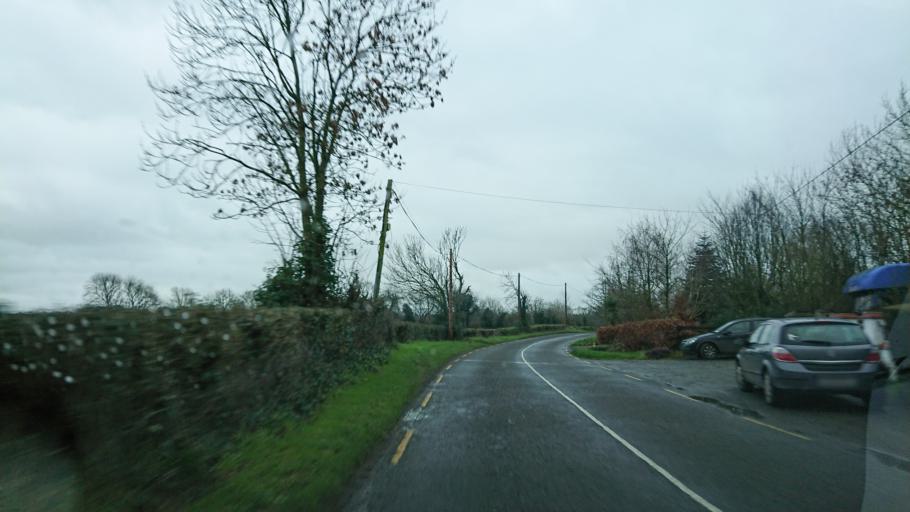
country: IE
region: Leinster
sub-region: Kilkenny
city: Callan
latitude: 52.5339
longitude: -7.2931
